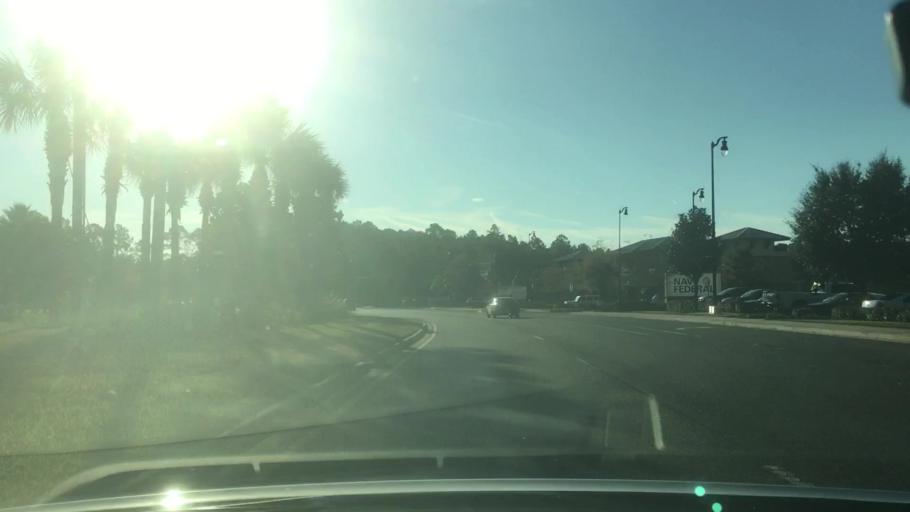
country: US
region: Florida
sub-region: Duval County
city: Jacksonville
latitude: 30.4779
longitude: -81.6350
